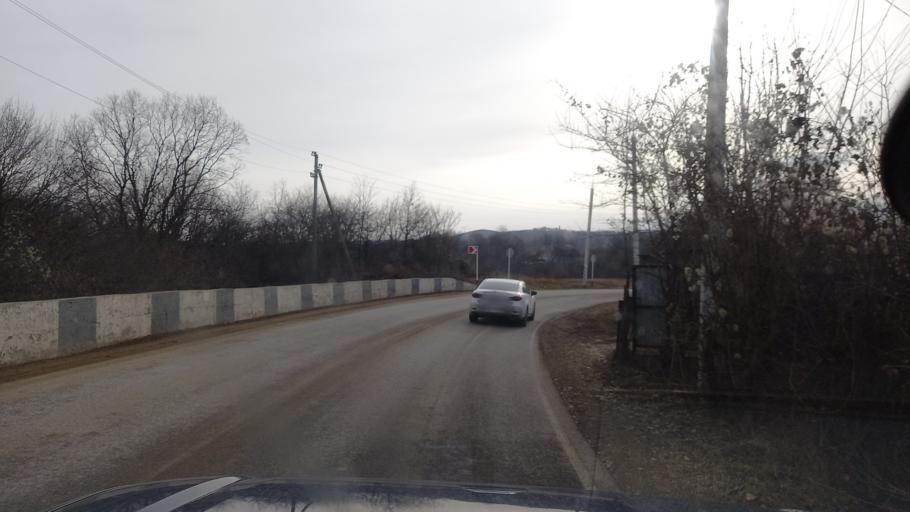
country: RU
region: Adygeya
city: Kamennomostskiy
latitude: 44.2963
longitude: 40.1907
